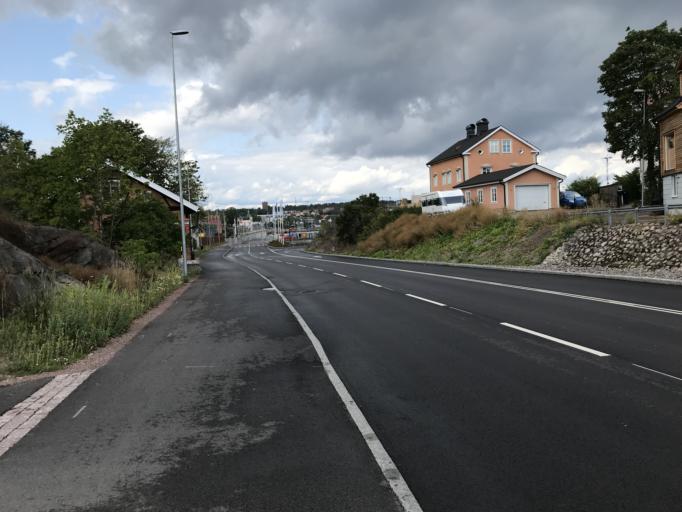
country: SE
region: Kalmar
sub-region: Oskarshamns Kommun
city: Oskarshamn
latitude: 57.2621
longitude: 16.4610
